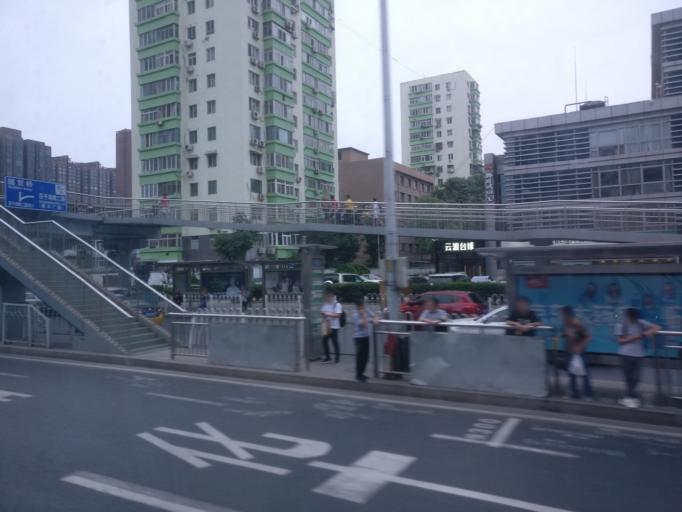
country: CN
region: Beijing
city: Longtan
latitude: 39.8953
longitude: 116.4555
